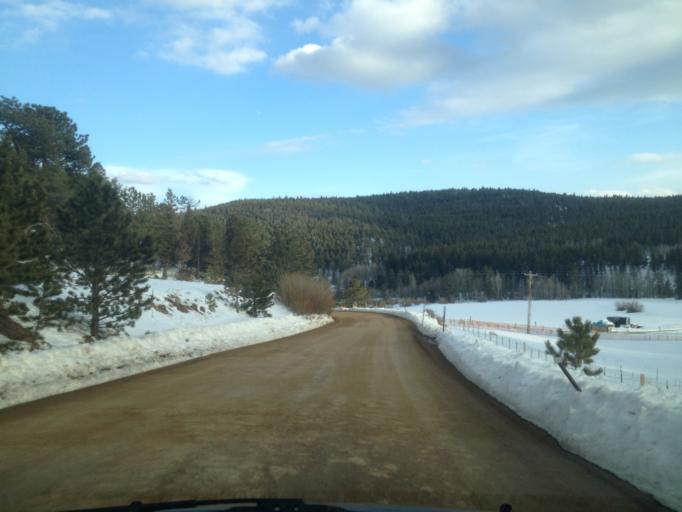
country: US
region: Colorado
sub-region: Boulder County
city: Nederland
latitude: 40.1237
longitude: -105.4542
